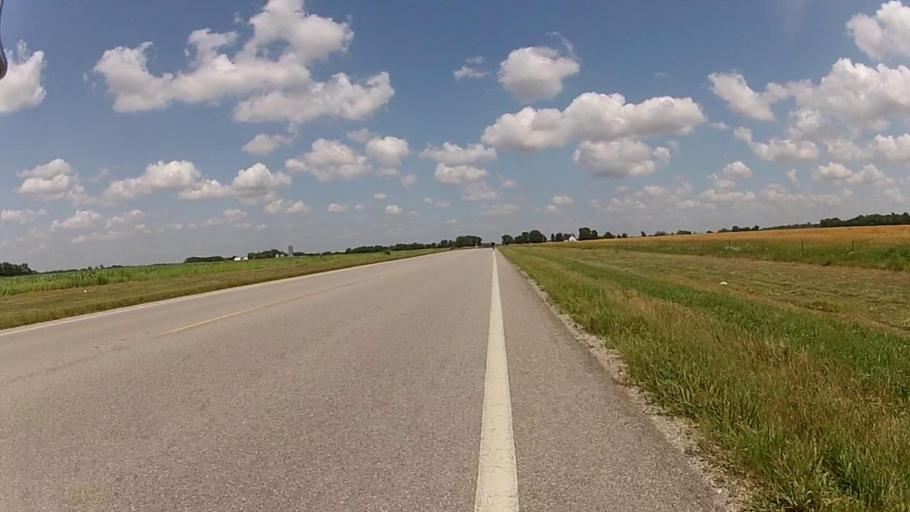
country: US
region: Kansas
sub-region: Labette County
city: Altamont
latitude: 37.1930
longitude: -95.2197
